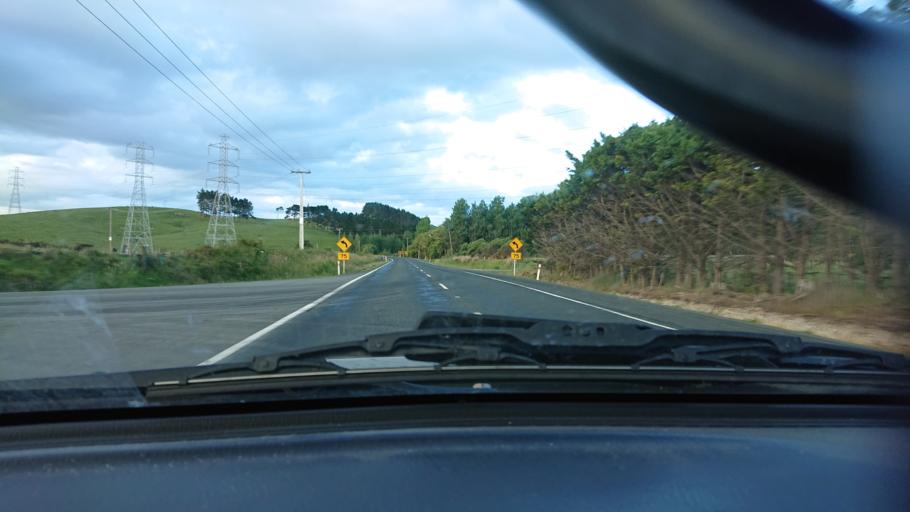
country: NZ
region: Auckland
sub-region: Auckland
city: Parakai
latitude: -36.4846
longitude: 174.4499
